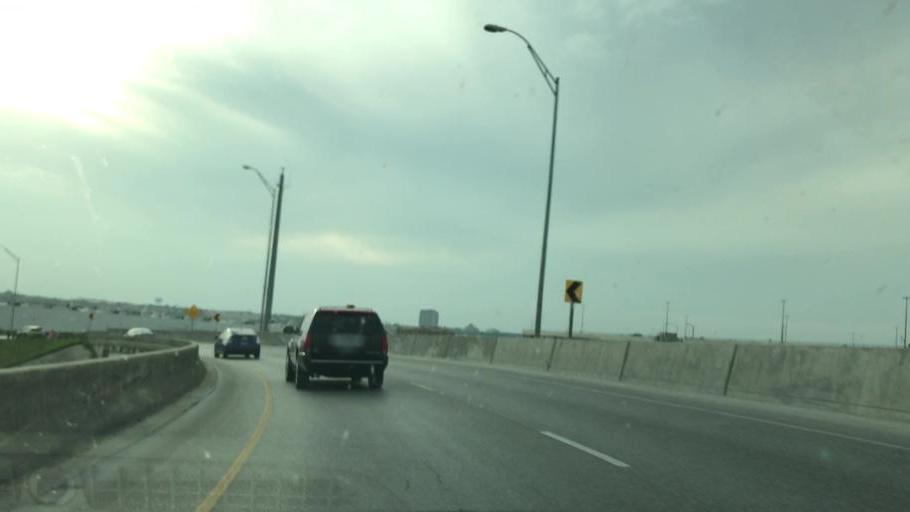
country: US
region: Texas
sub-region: Bexar County
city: Kirby
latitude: 29.4564
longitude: -98.4144
